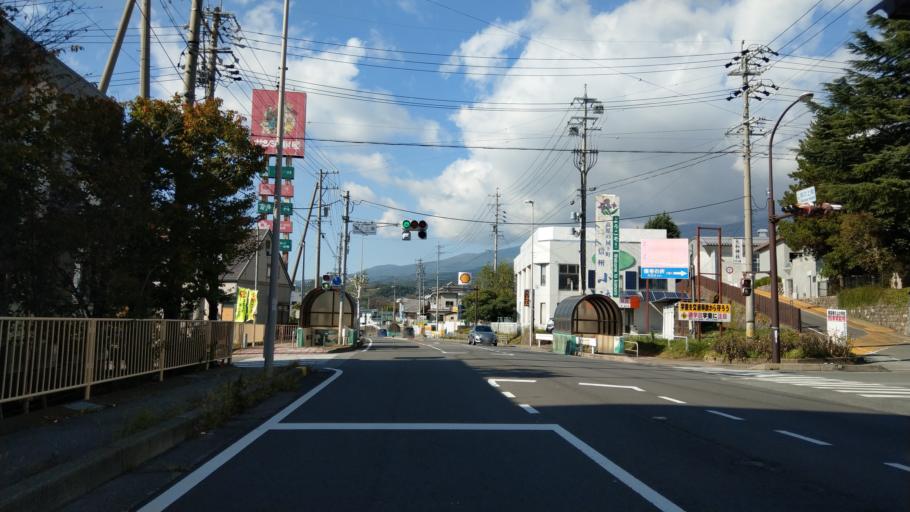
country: JP
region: Nagano
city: Komoro
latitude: 36.3283
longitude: 138.4338
